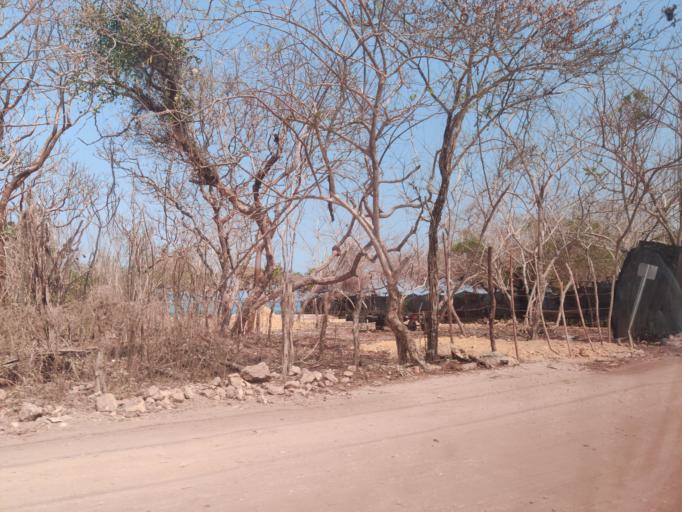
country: CO
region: Bolivar
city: Turbana
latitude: 10.1832
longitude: -75.6438
